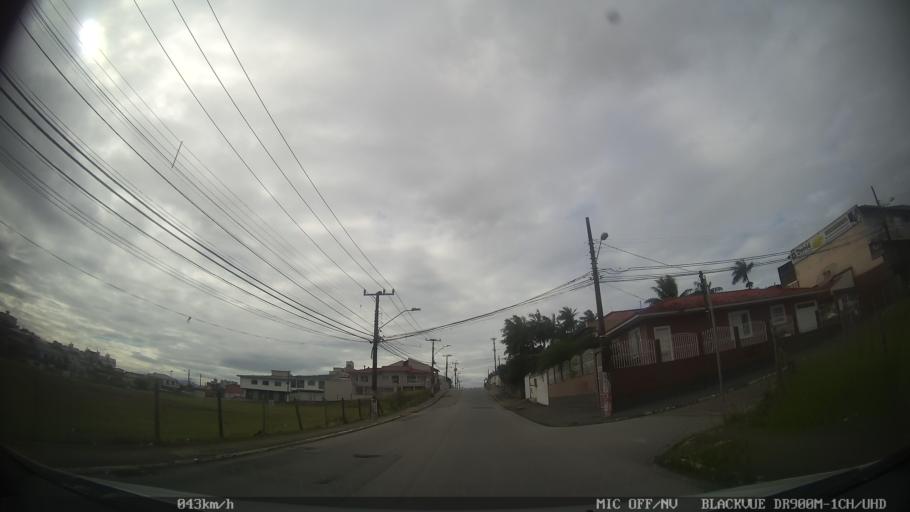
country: BR
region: Santa Catarina
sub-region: Sao Jose
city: Campinas
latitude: -27.5671
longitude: -48.6287
